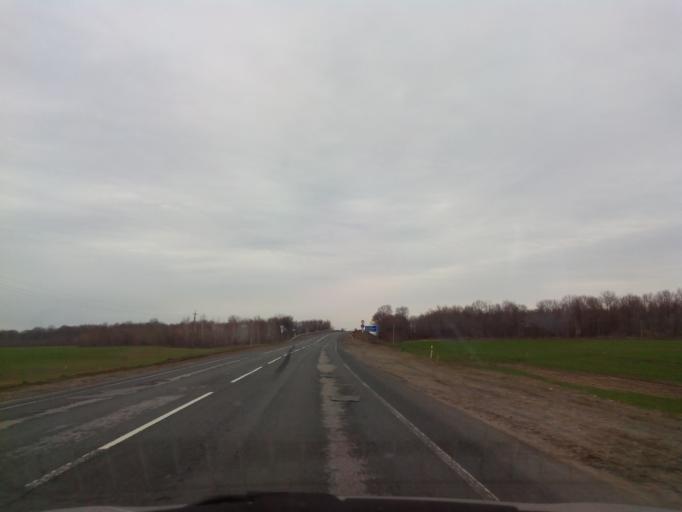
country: RU
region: Tambov
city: Zavoronezhskoye
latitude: 52.9131
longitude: 40.6298
